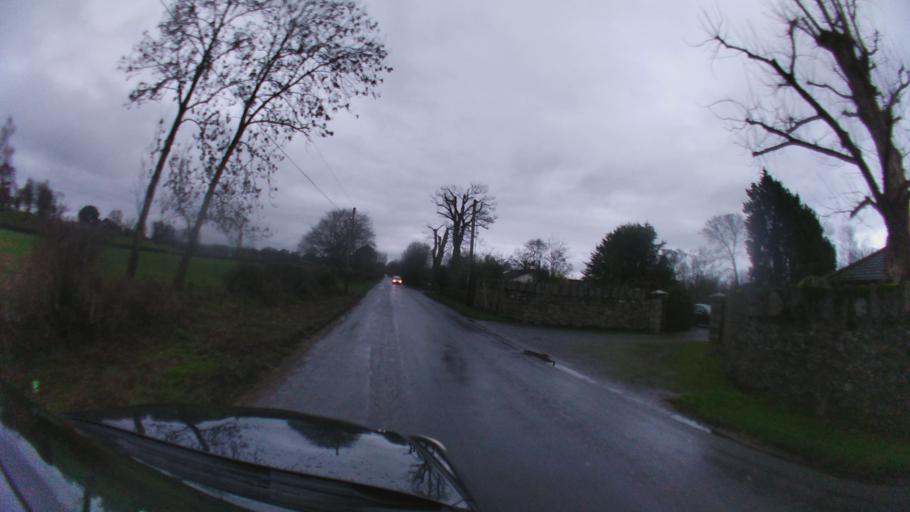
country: IE
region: Leinster
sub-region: County Carlow
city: Bagenalstown
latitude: 52.6506
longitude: -6.9891
